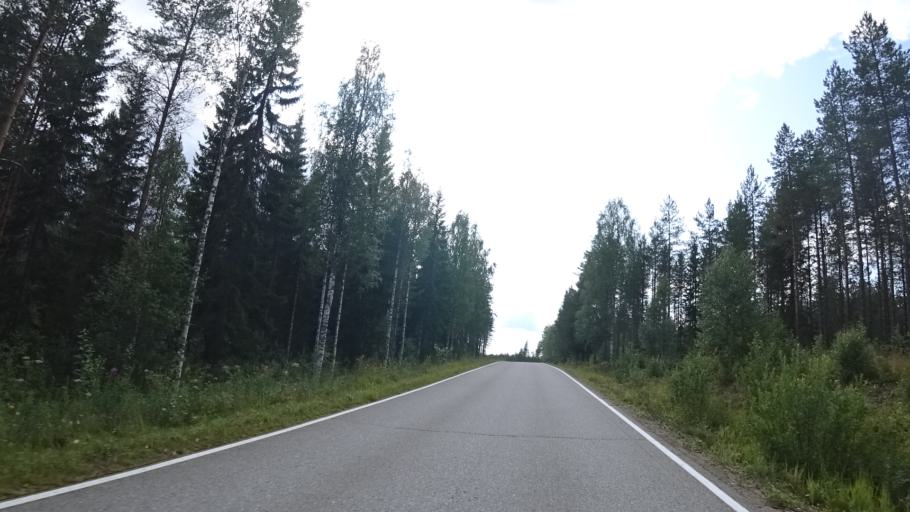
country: FI
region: North Karelia
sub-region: Joensuu
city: Ilomantsi
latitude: 62.4211
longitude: 31.0225
